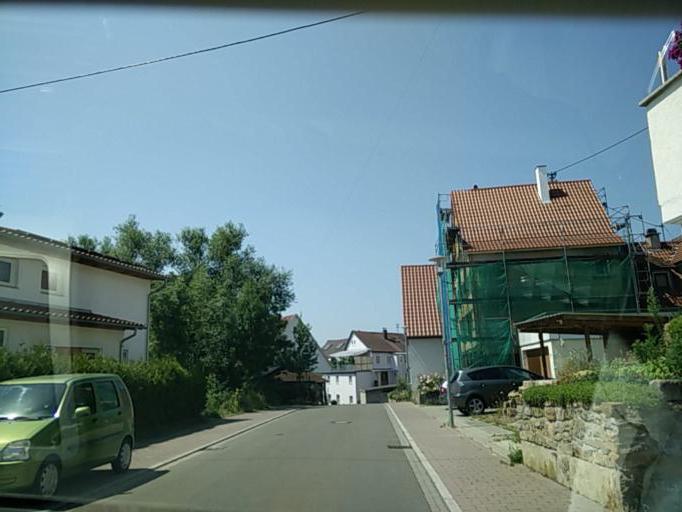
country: DE
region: Baden-Wuerttemberg
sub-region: Tuebingen Region
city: Gomaringen
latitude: 48.4545
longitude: 9.1013
